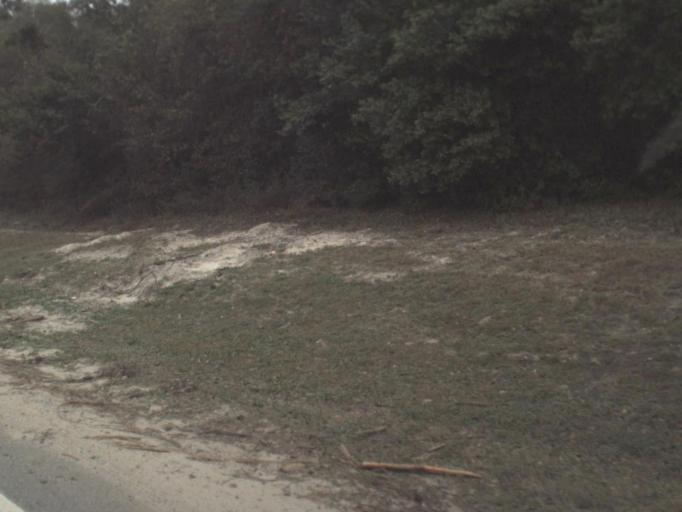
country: US
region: Florida
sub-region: Bay County
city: Parker
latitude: 30.1391
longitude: -85.6156
